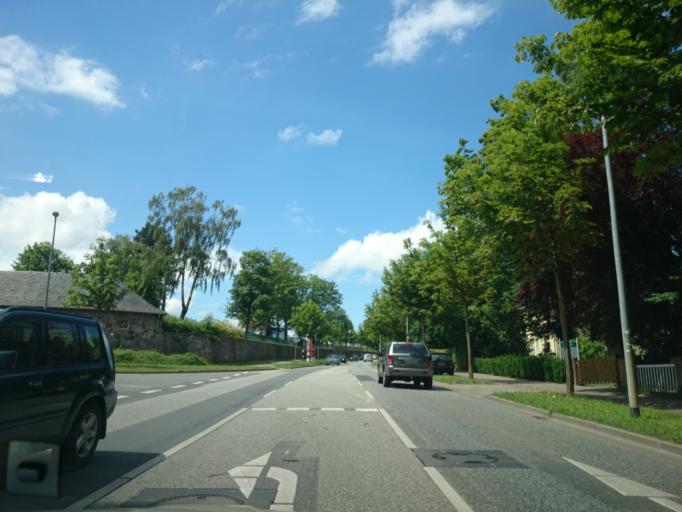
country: DE
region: Mecklenburg-Vorpommern
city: Wismar
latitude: 53.8943
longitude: 11.4337
